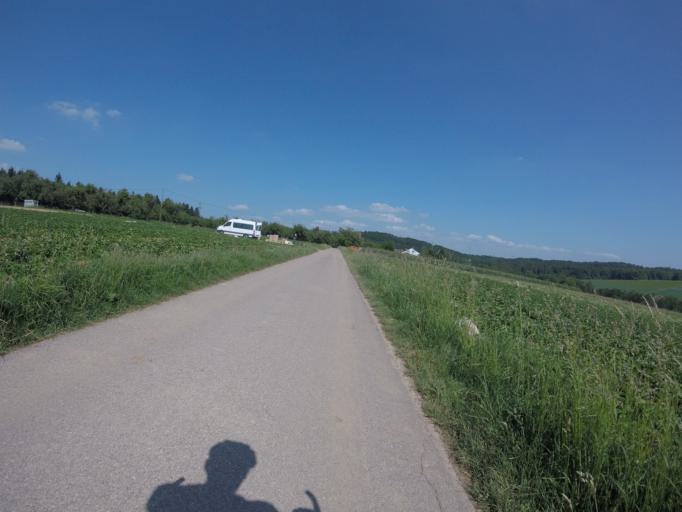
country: DE
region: Baden-Wuerttemberg
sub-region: Regierungsbezirk Stuttgart
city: Kirchberg an der Murr
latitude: 48.9727
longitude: 9.3195
